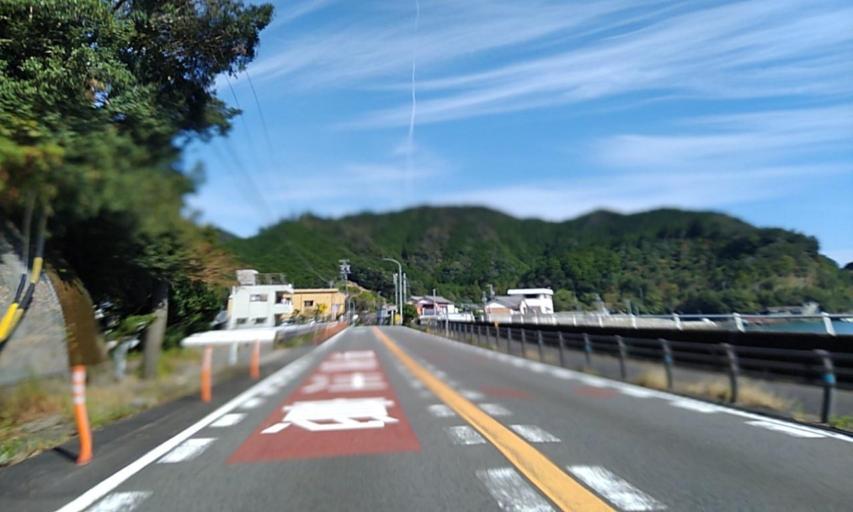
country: JP
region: Mie
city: Owase
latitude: 34.1625
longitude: 136.2789
